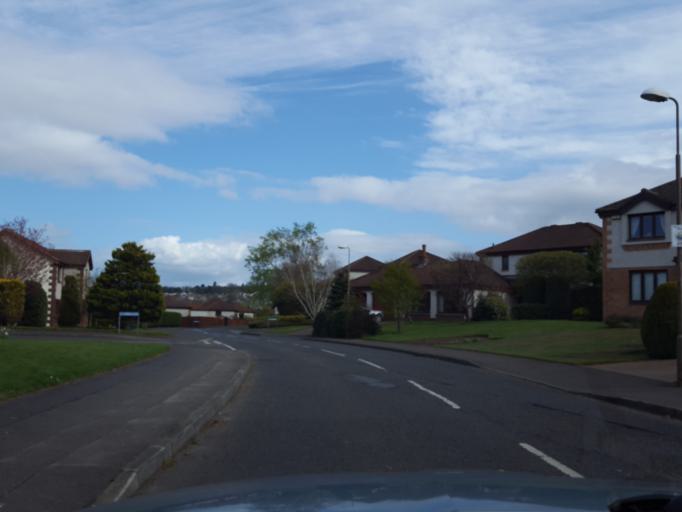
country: GB
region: Scotland
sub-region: West Lothian
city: Linlithgow
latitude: 55.9705
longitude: -3.6249
